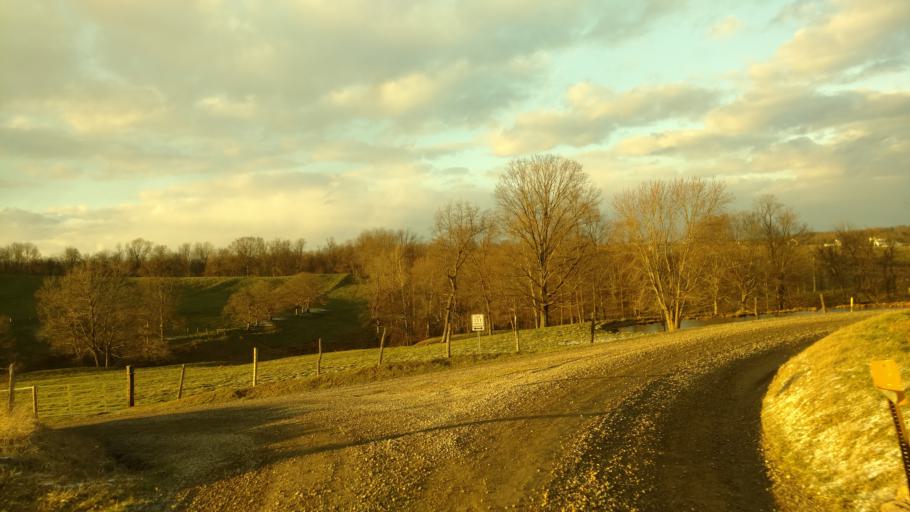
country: US
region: Ohio
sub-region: Tuscarawas County
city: Sugarcreek
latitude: 40.5151
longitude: -81.7693
